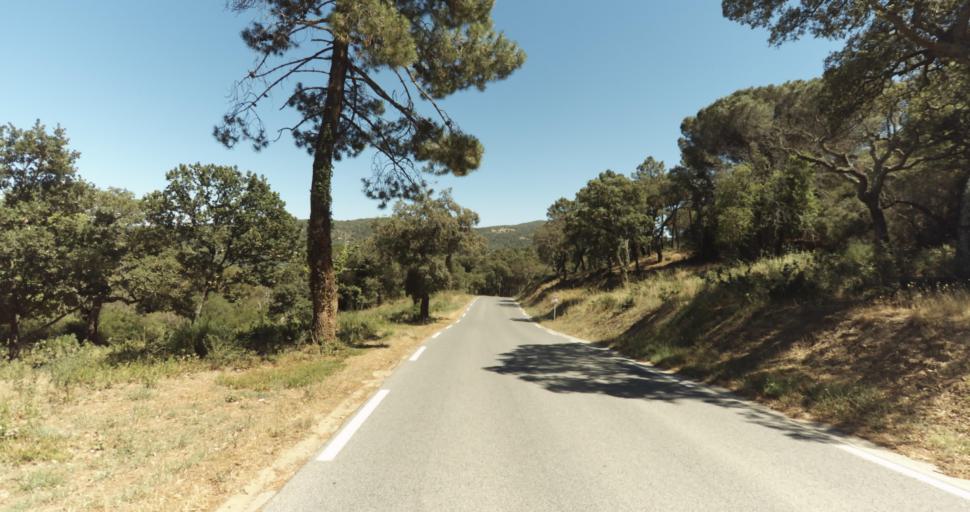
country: FR
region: Provence-Alpes-Cote d'Azur
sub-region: Departement du Var
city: Gassin
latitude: 43.2420
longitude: 6.5619
